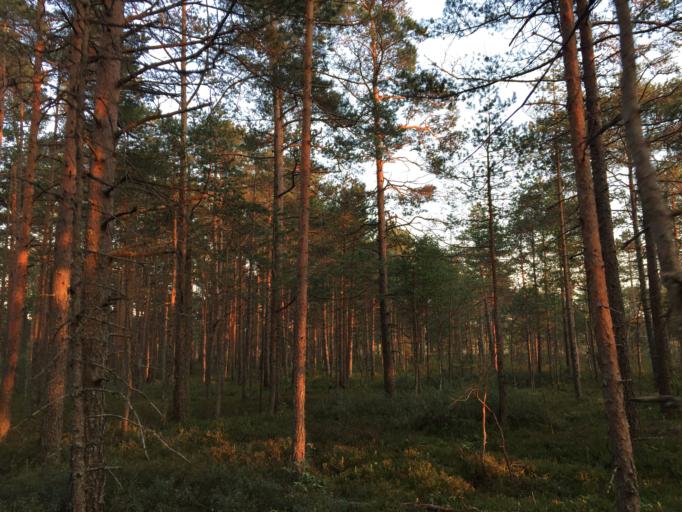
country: LV
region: Limbazu Rajons
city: Limbazi
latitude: 57.5729
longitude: 24.7878
